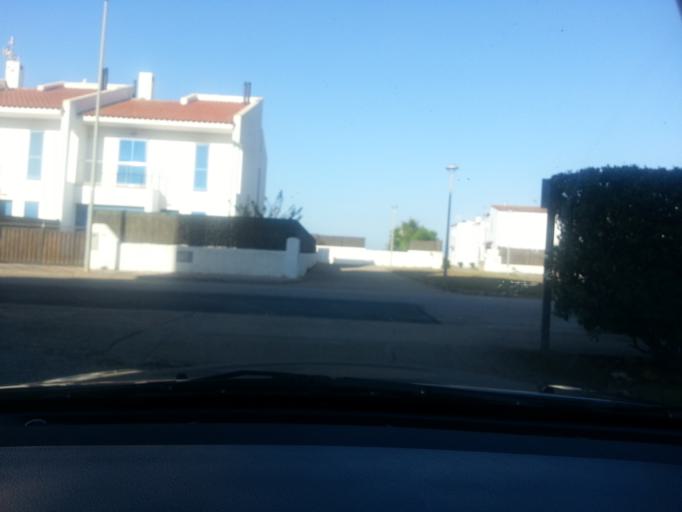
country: ES
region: Catalonia
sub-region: Provincia de Girona
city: Pals
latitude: 42.0094
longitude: 3.1937
